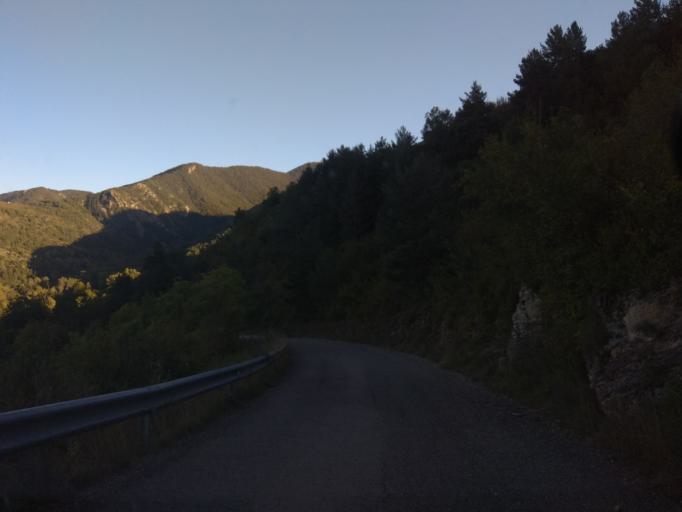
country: ES
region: Catalonia
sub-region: Provincia de Lleida
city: Lles de Cerdanya
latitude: 42.3530
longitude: 1.7194
